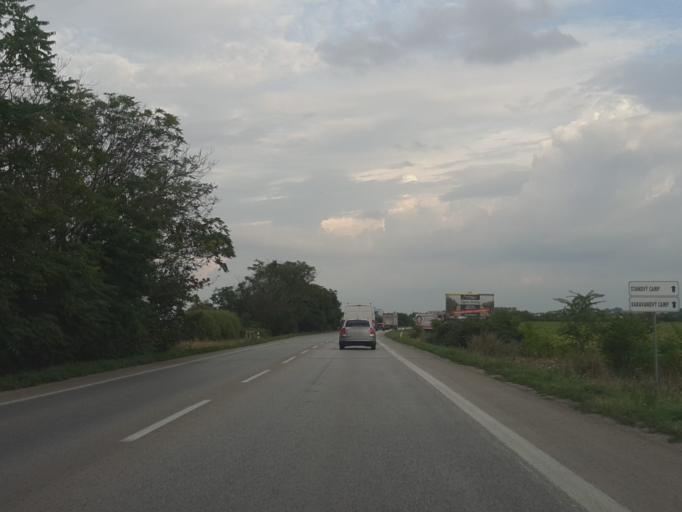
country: SK
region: Bratislavsky
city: Senec
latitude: 48.2291
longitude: 17.3770
